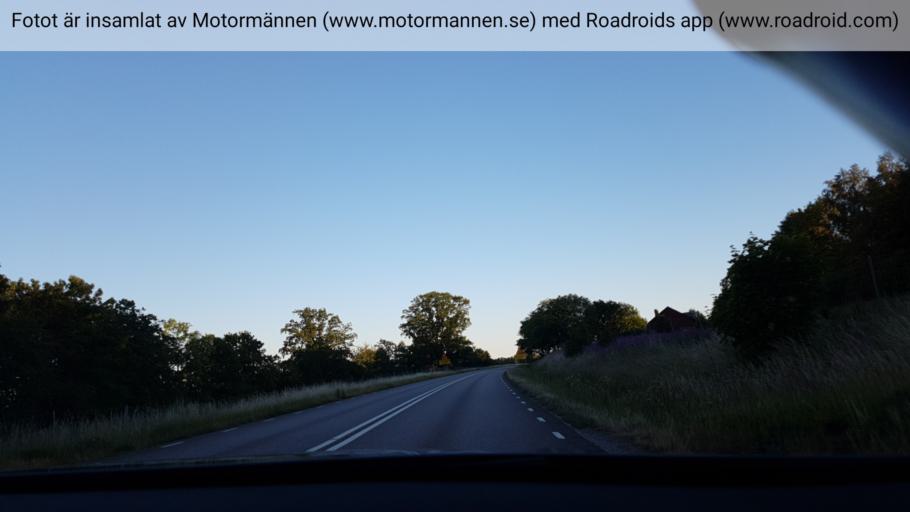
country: SE
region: Vaestra Goetaland
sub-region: Hjo Kommun
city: Hjo
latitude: 58.3339
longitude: 14.3354
